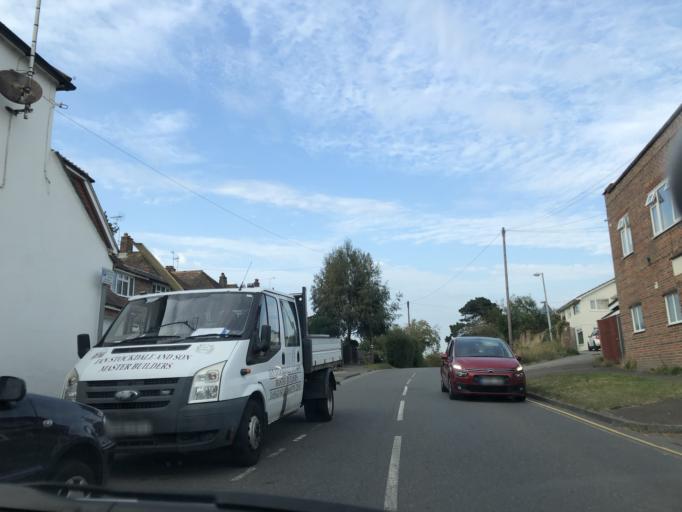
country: GB
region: England
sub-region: East Sussex
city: Bexhill-on-Sea
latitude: 50.8456
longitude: 0.4341
